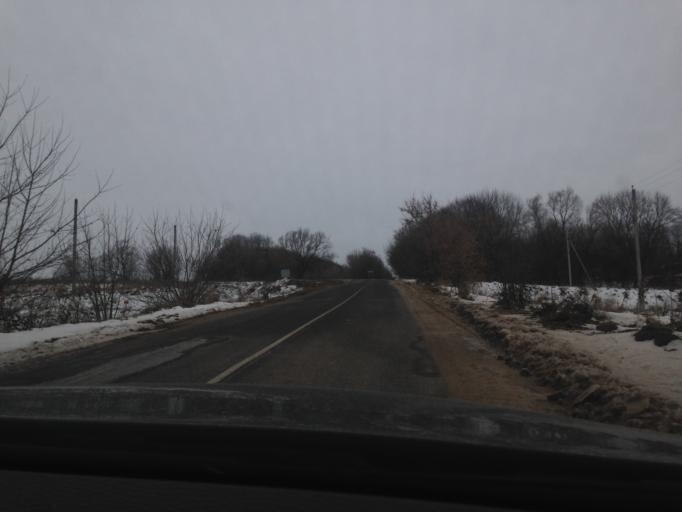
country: RU
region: Tula
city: Teploye
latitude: 53.7761
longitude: 37.6382
